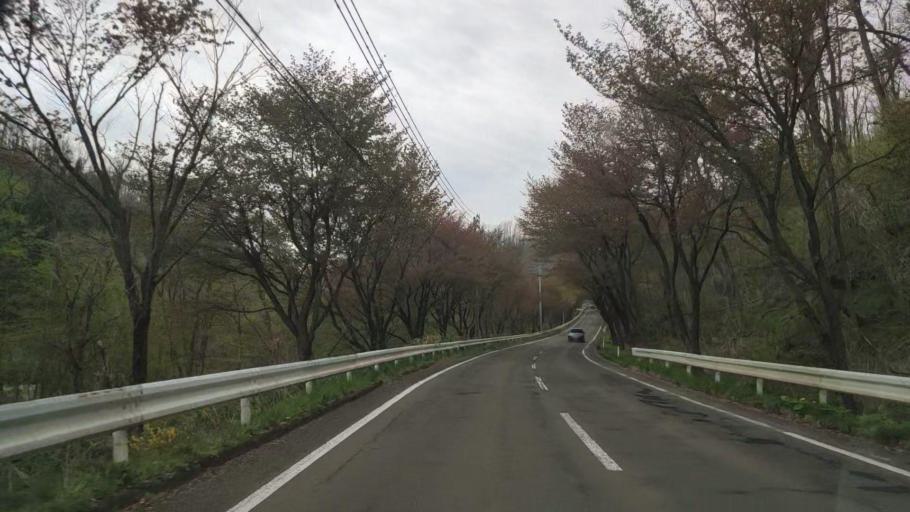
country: JP
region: Akita
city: Hanawa
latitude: 40.3441
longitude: 140.7718
